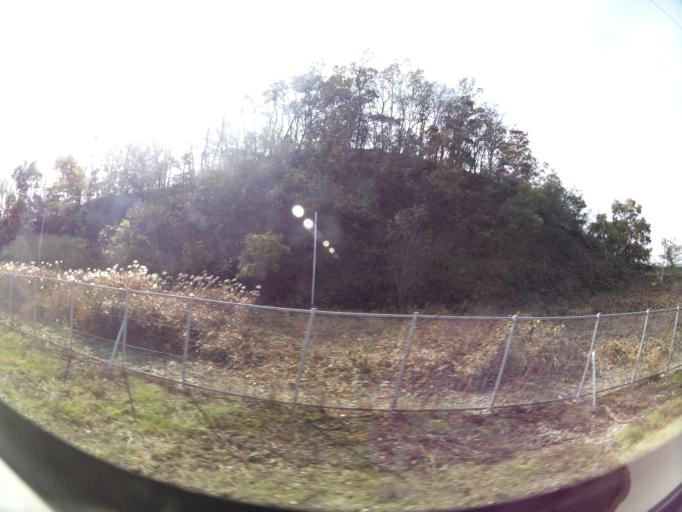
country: KR
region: Chungcheongbuk-do
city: Cheongju-si
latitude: 36.6351
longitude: 127.2878
